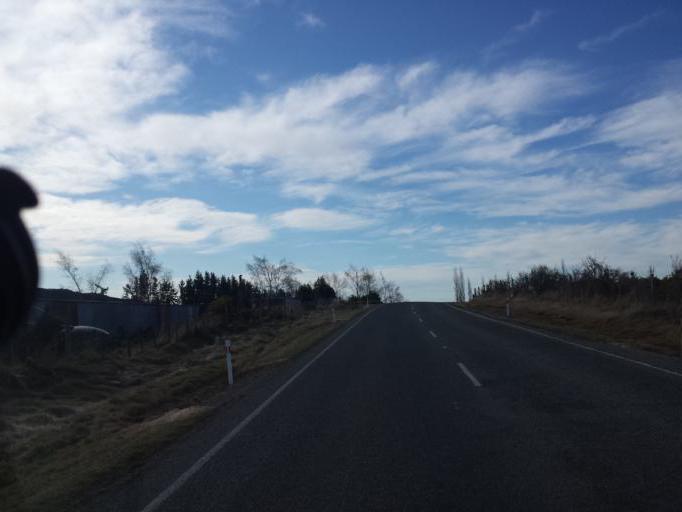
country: NZ
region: Canterbury
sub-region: Timaru District
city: Pleasant Point
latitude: -44.1238
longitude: 171.1041
